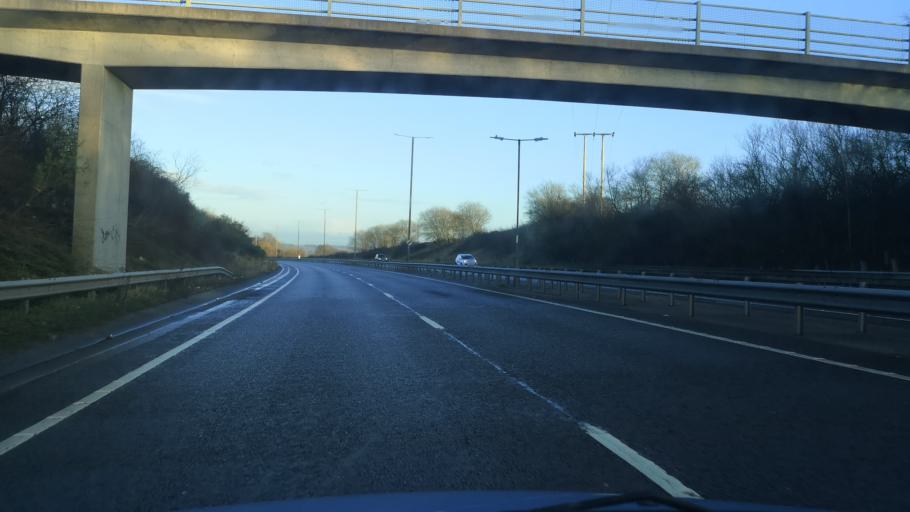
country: GB
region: England
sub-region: Barnsley
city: Hoyland Nether
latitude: 53.5102
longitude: -1.4246
